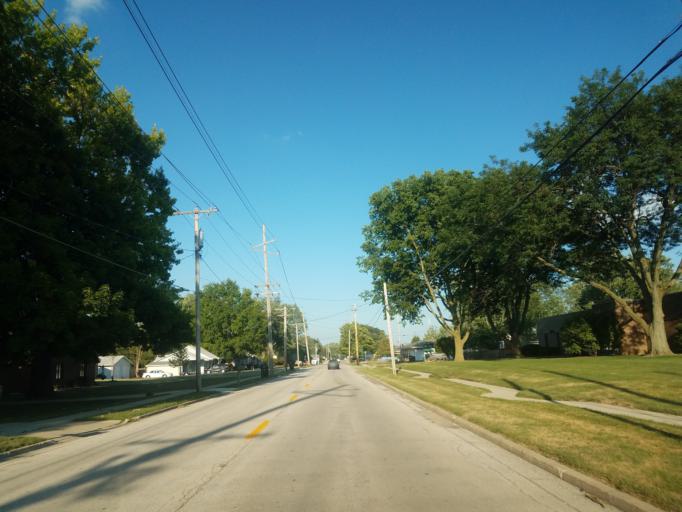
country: US
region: Illinois
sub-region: McLean County
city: Bloomington
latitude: 40.4635
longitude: -88.9791
